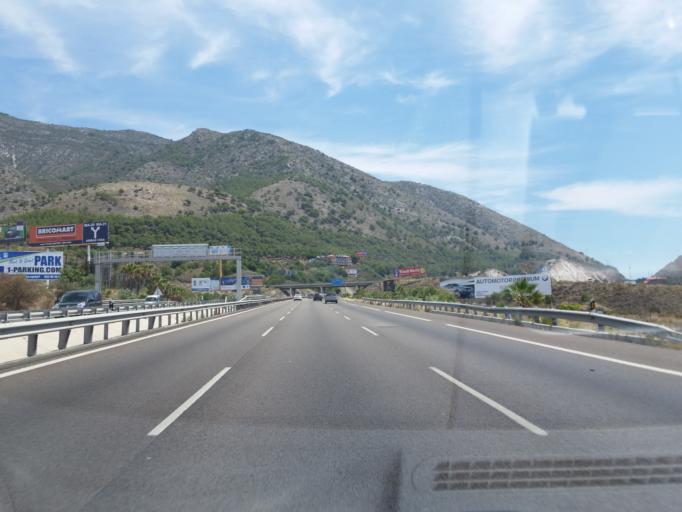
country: ES
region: Andalusia
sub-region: Provincia de Malaga
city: Mijas
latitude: 36.5822
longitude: -4.6059
